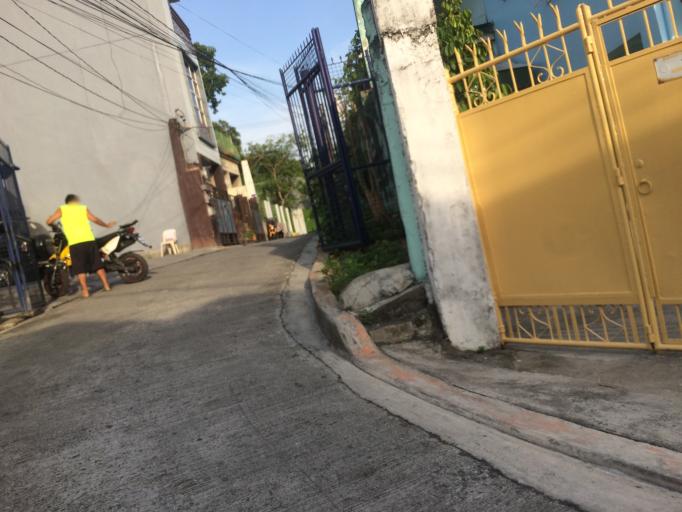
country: PH
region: Calabarzon
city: Bagong Pagasa
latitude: 14.6695
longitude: 121.0178
